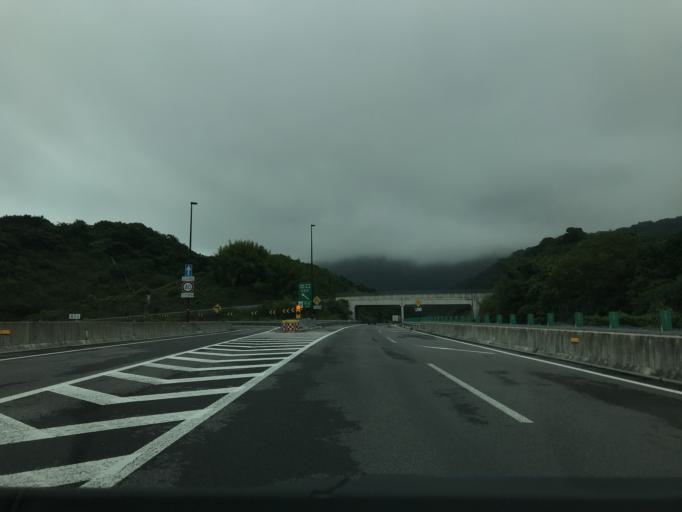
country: JP
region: Oita
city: Bungo-Takada-shi
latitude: 33.4991
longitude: 131.3166
